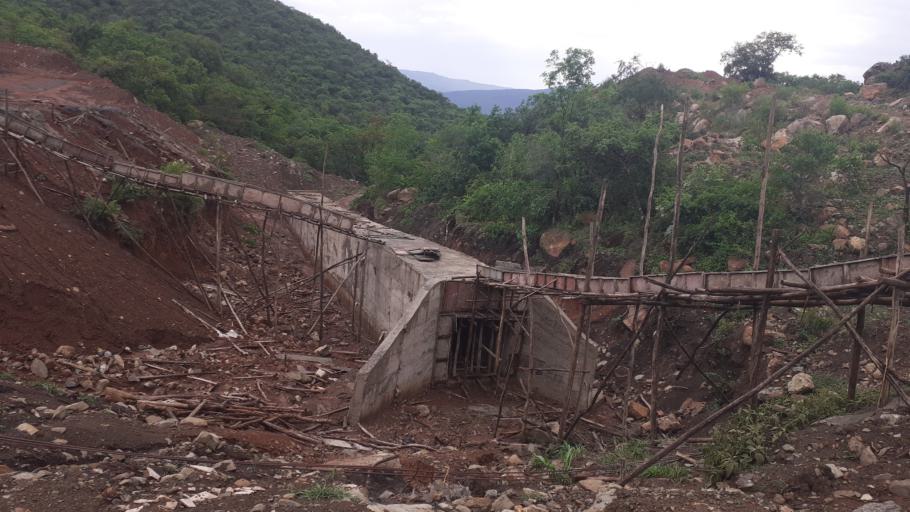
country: ET
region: Southern Nations, Nationalities, and People's Region
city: Areka
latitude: 7.5833
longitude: 37.5108
